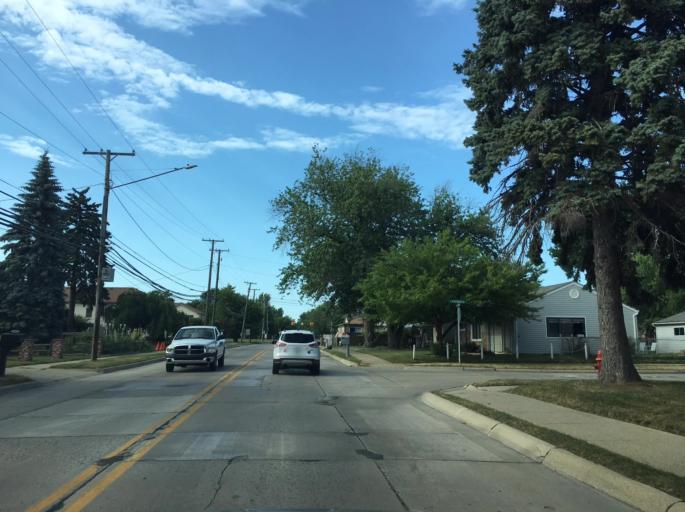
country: US
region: Michigan
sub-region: Macomb County
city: Fraser
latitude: 42.5376
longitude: -82.9195
